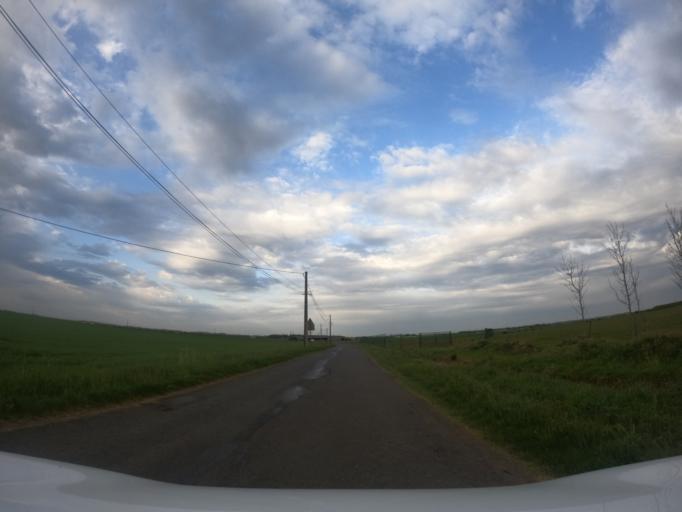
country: FR
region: Pays de la Loire
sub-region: Departement de la Vendee
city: Fontenay-le-Comte
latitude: 46.4353
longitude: -0.7922
